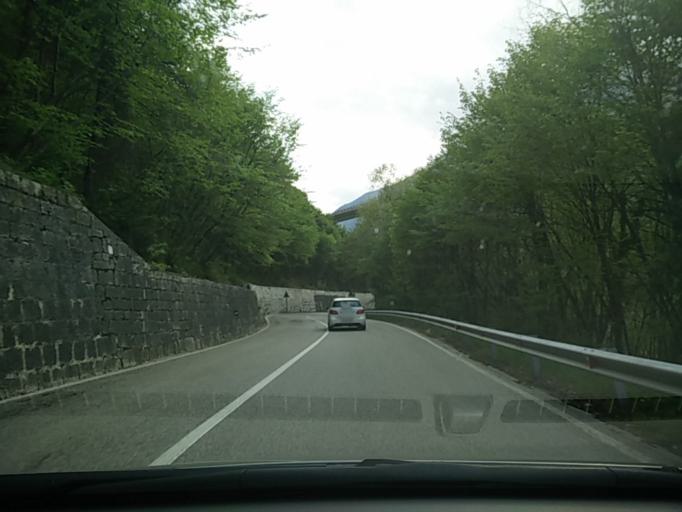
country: IT
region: Veneto
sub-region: Provincia di Belluno
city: Farra d'Alpago
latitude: 46.0704
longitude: 12.3406
